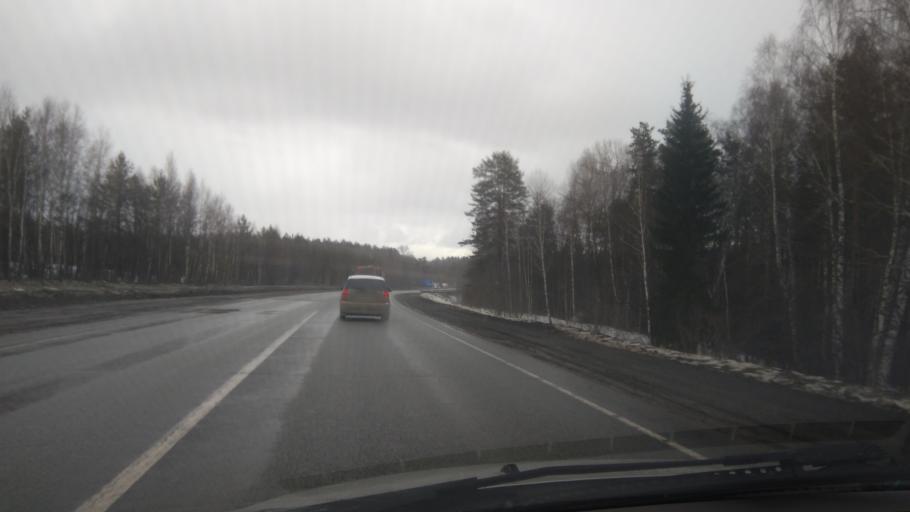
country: RU
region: Sverdlovsk
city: Ufimskiy
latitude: 56.7798
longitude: 58.2599
